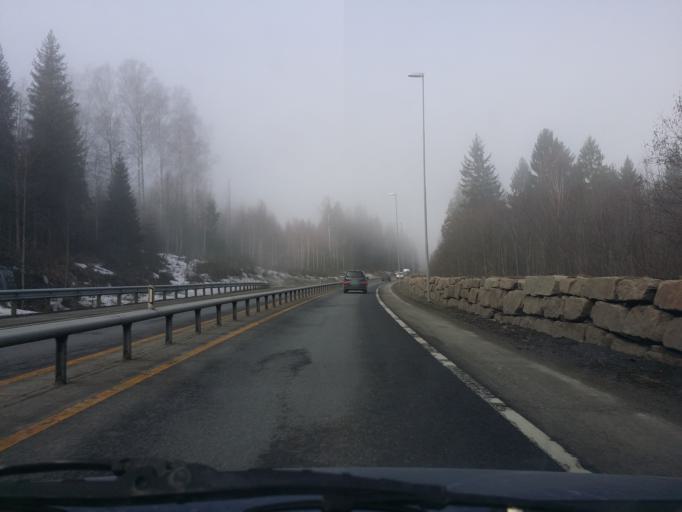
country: NO
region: Buskerud
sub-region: Drammen
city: Drammen
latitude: 59.7404
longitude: 10.1419
